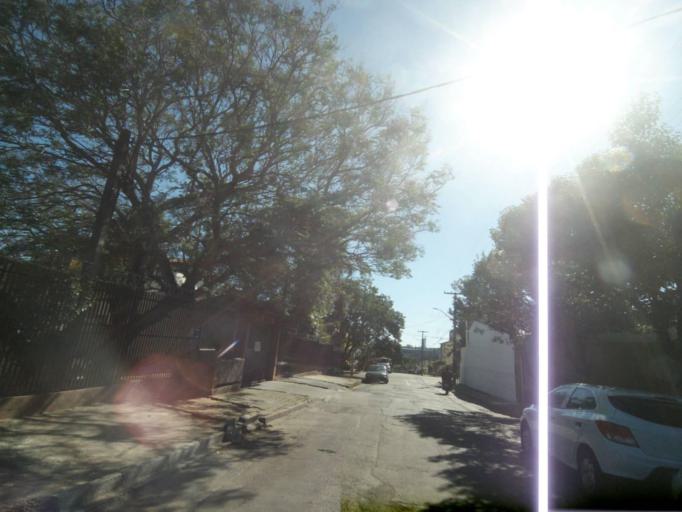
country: BR
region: Parana
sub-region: Curitiba
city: Curitiba
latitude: -25.4528
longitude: -49.3529
